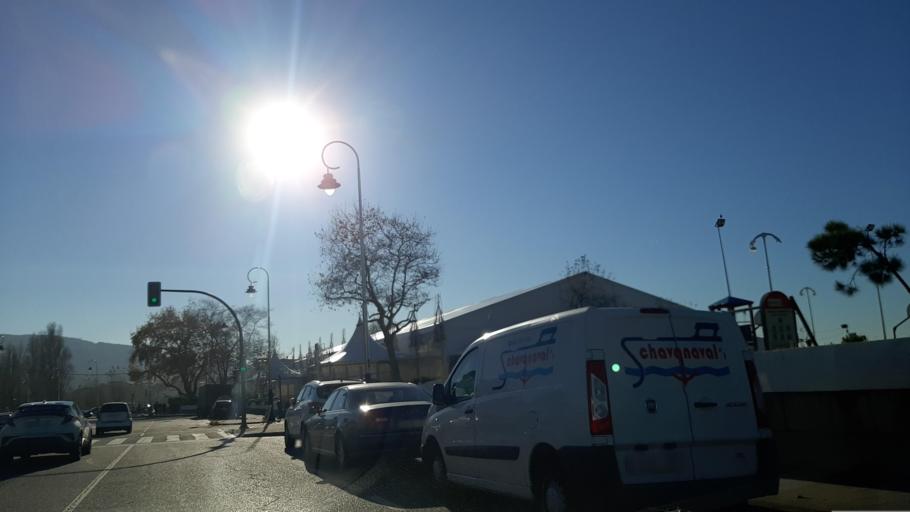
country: ES
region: Galicia
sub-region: Provincia de Pontevedra
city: Cangas
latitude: 42.2066
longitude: -8.7766
